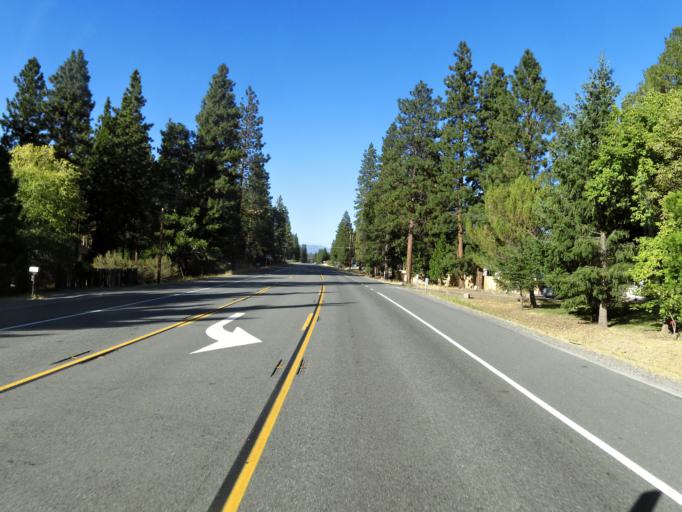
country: US
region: California
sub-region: Siskiyou County
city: Weed
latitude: 41.4488
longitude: -122.3635
